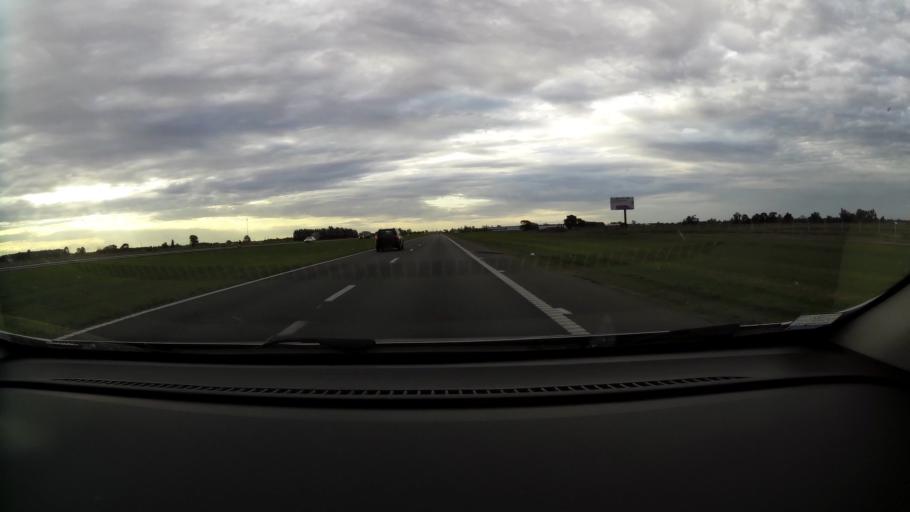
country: AR
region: Buenos Aires
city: San Nicolas de los Arroyos
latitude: -33.3981
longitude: -60.2074
